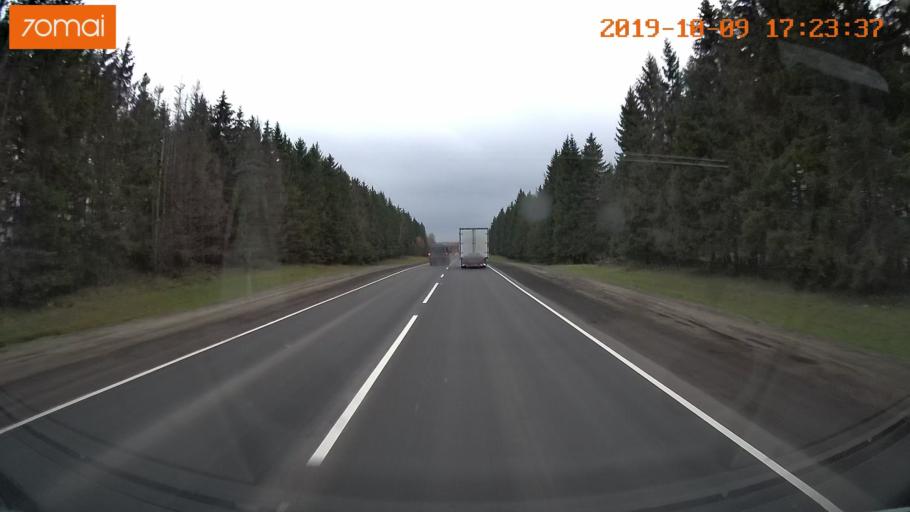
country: RU
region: Ivanovo
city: Furmanov
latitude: 57.1941
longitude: 41.1152
